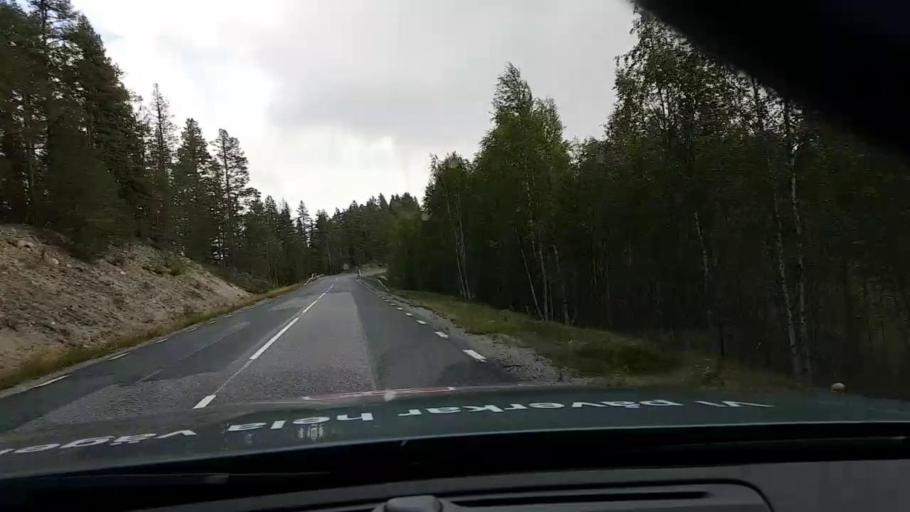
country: SE
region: Vaesterbotten
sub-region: Asele Kommun
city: Asele
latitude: 63.8392
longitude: 17.4320
